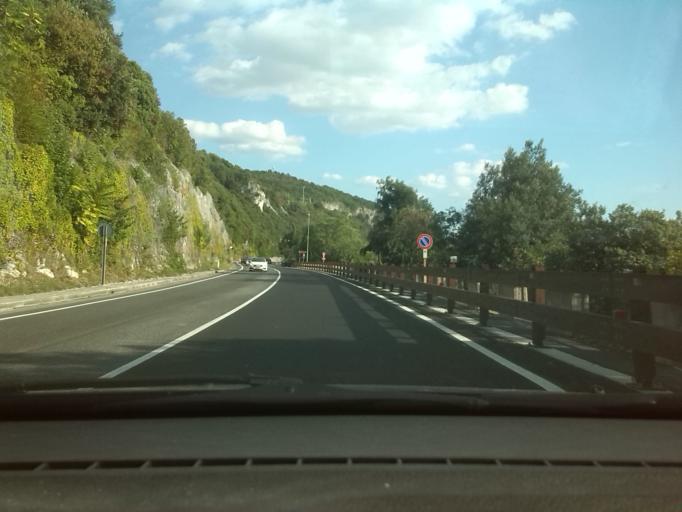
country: IT
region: Friuli Venezia Giulia
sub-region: Provincia di Trieste
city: Aurisina Cave
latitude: 45.7523
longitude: 13.6538
